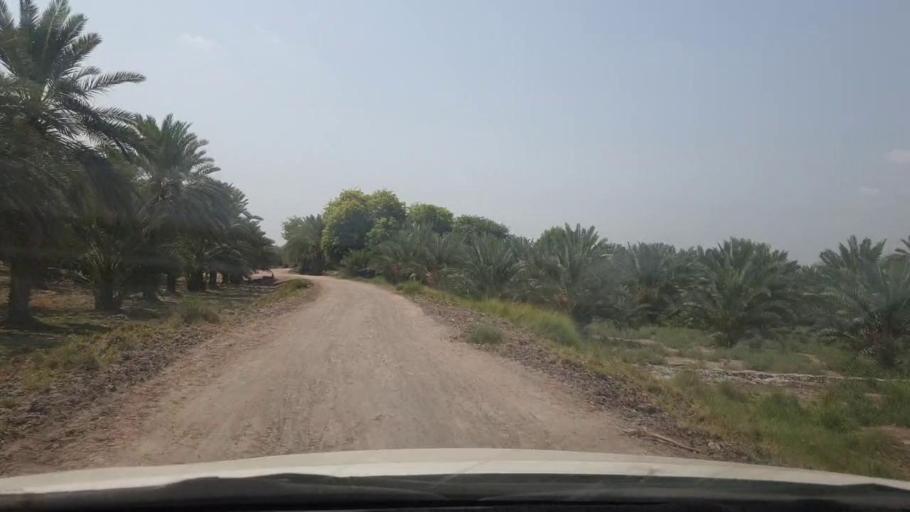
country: PK
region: Sindh
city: Khairpur
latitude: 27.5613
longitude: 68.8480
